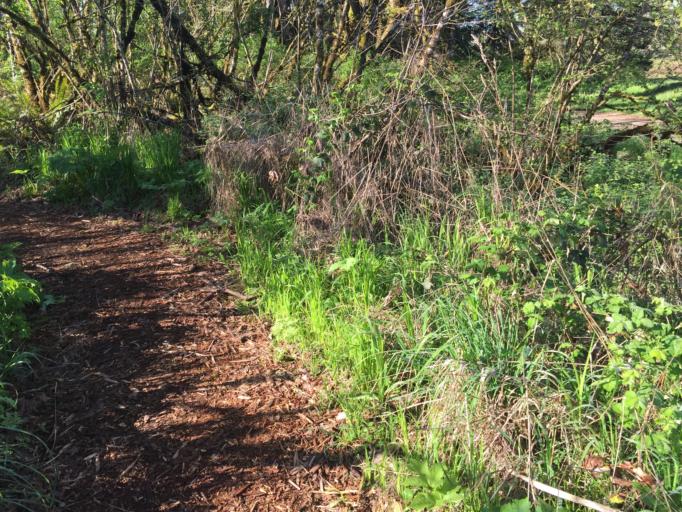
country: US
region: Oregon
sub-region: Lane County
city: Springfield
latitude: 44.0025
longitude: -122.9805
